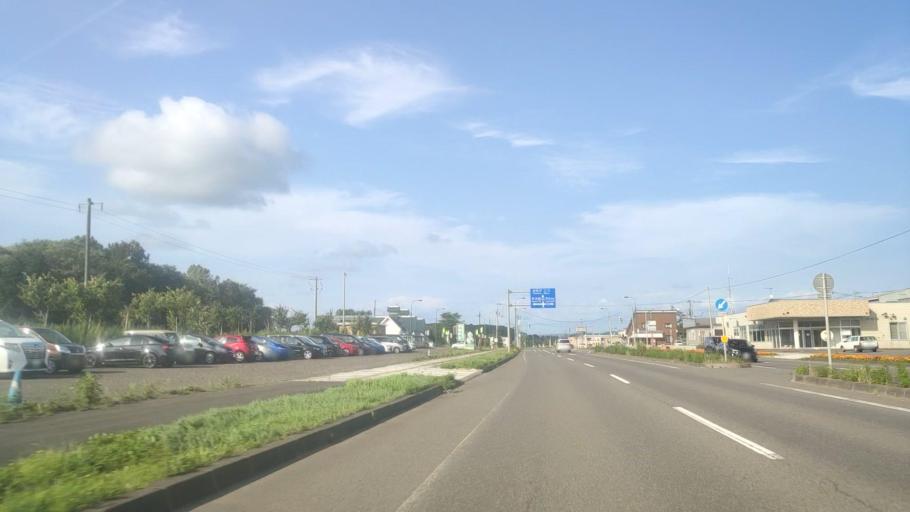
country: JP
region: Hokkaido
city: Chitose
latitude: 42.7642
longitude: 141.8133
